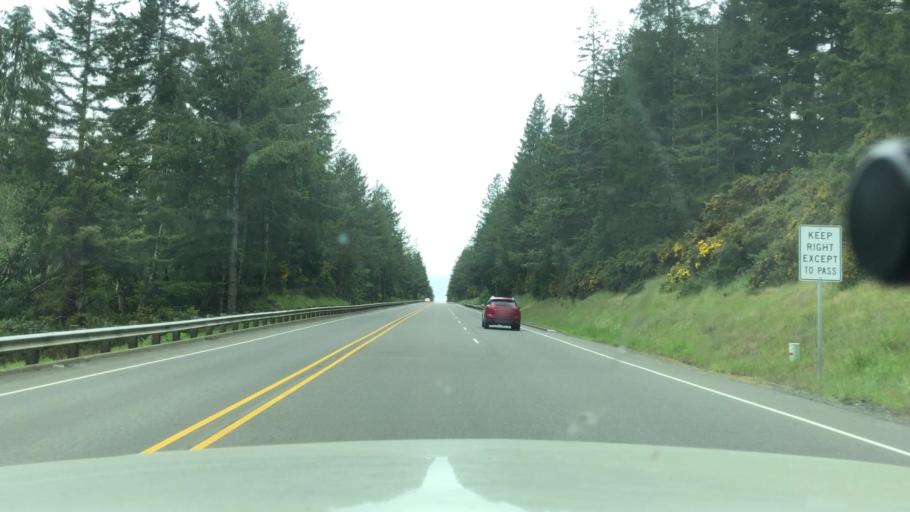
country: US
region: Oregon
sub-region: Coos County
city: Bandon
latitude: 43.1920
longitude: -124.3495
